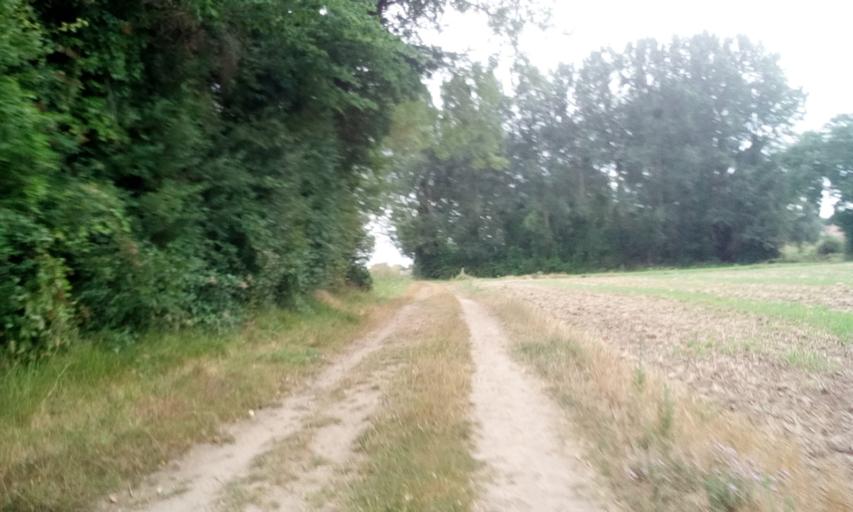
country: FR
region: Lower Normandy
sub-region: Departement du Calvados
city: Bellengreville
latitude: 49.1119
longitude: -0.1977
